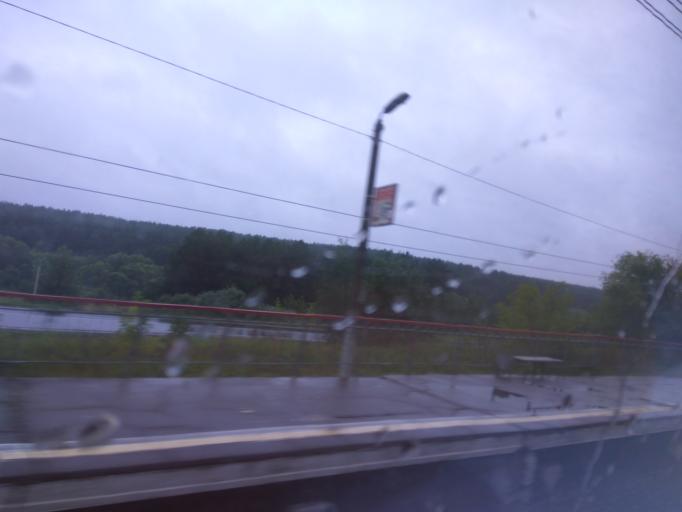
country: RU
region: Moskovskaya
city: Kashira
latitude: 54.8733
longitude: 38.1197
